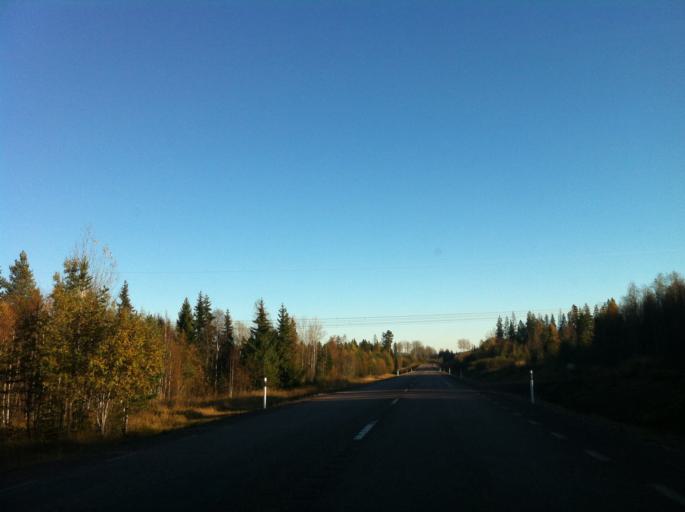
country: SE
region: Dalarna
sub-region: Rattviks Kommun
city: Raettvik
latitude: 60.8375
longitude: 15.2207
